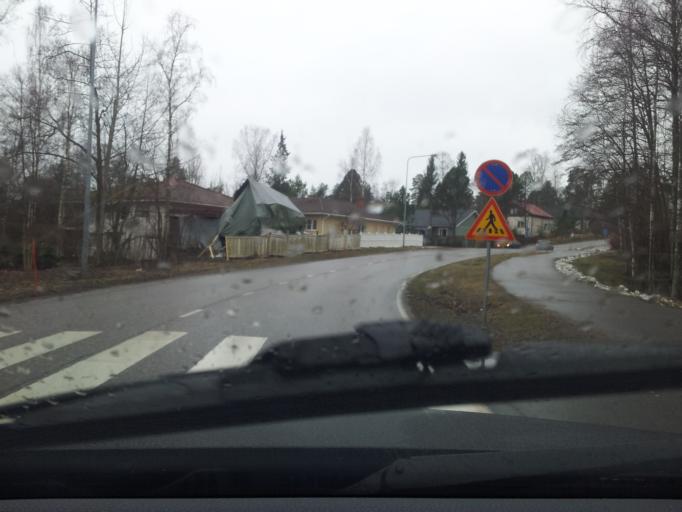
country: FI
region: Uusimaa
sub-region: Helsinki
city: Espoo
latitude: 60.1636
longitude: 24.6808
